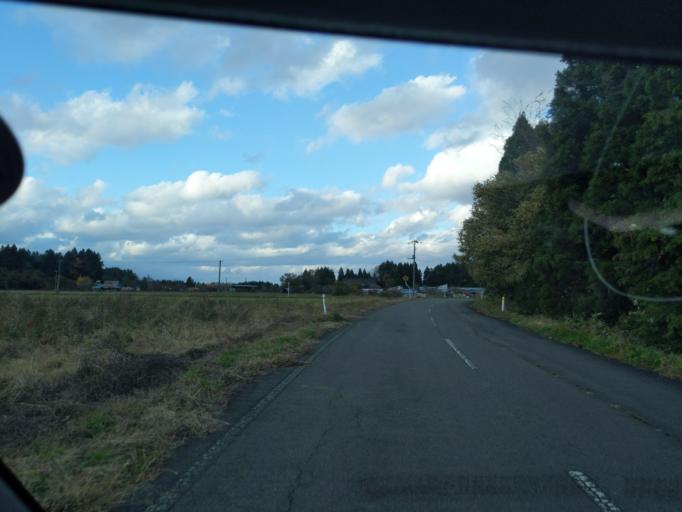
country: JP
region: Iwate
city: Mizusawa
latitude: 39.0967
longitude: 141.0135
